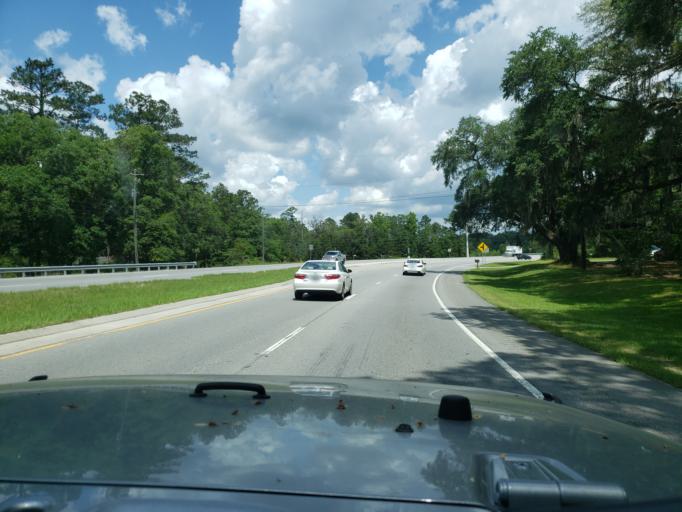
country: US
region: Georgia
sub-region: Chatham County
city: Georgetown
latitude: 32.0459
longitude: -81.2138
